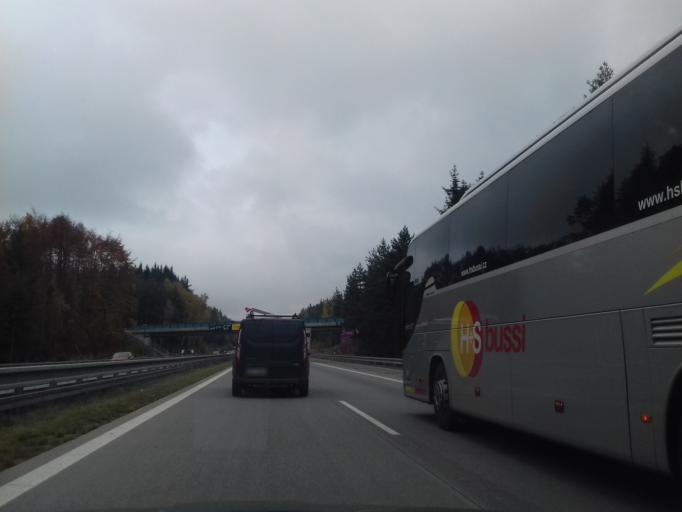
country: CZ
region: Central Bohemia
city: Cechtice
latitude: 49.6251
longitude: 15.1323
